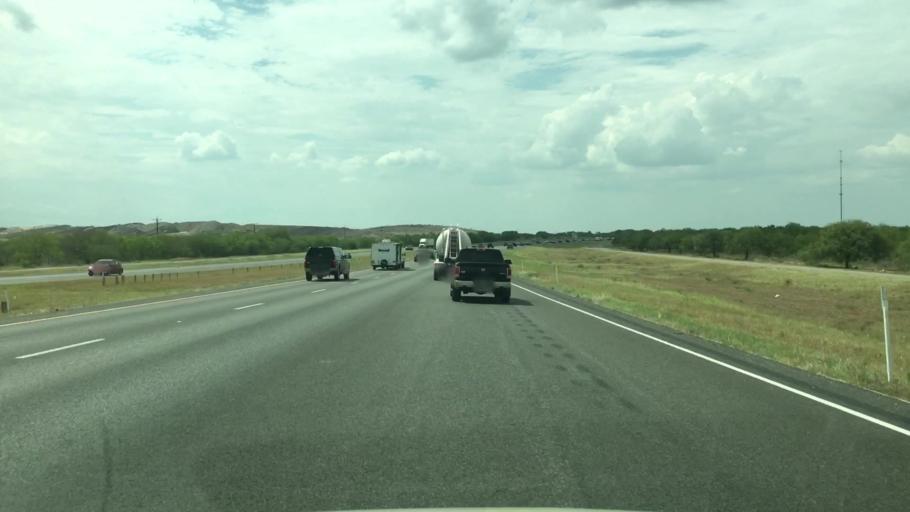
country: US
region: Texas
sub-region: Atascosa County
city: Pleasanton
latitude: 28.7870
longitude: -98.3250
